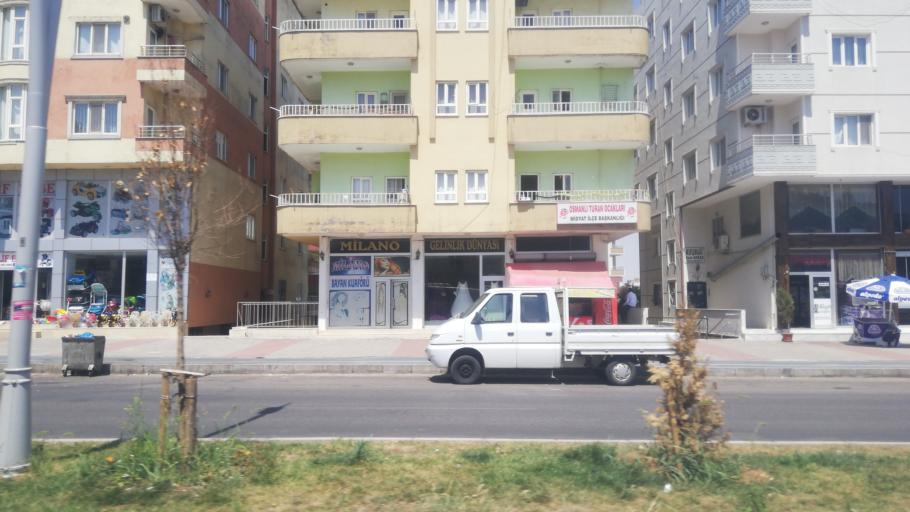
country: TR
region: Mardin
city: Midyat
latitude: 37.4173
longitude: 41.3616
